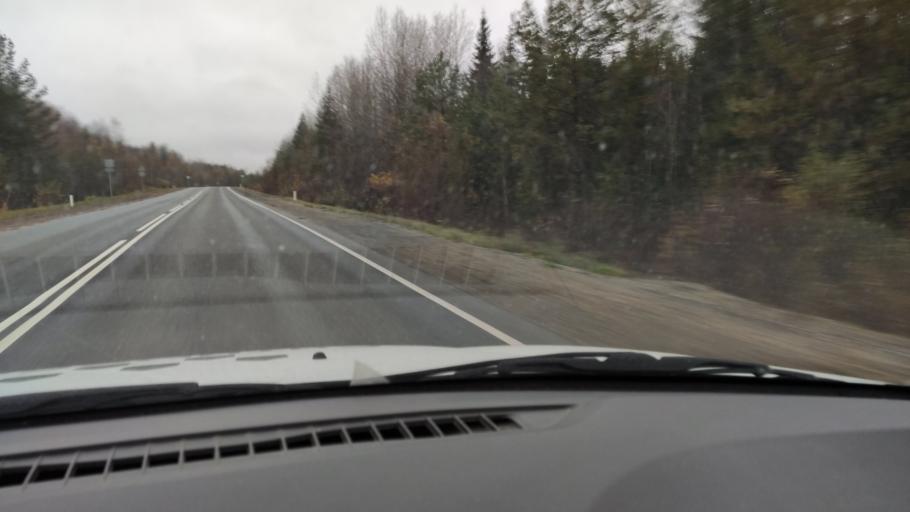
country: RU
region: Kirov
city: Omutninsk
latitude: 58.7003
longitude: 52.1157
